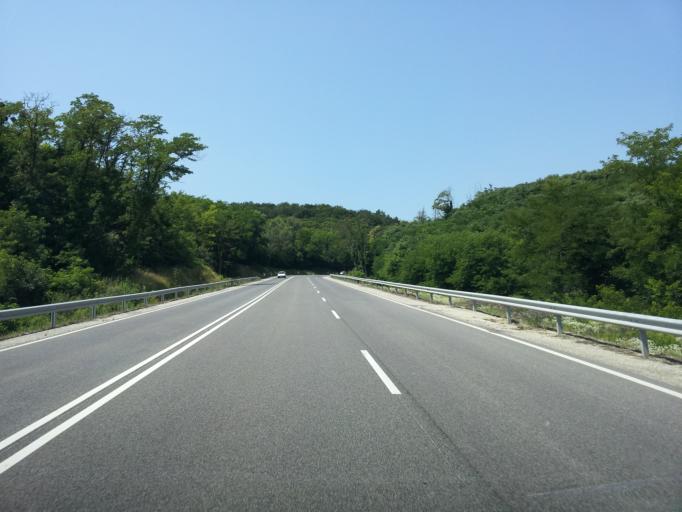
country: HU
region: Zala
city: Zalaegerszeg
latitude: 46.8468
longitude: 16.9150
